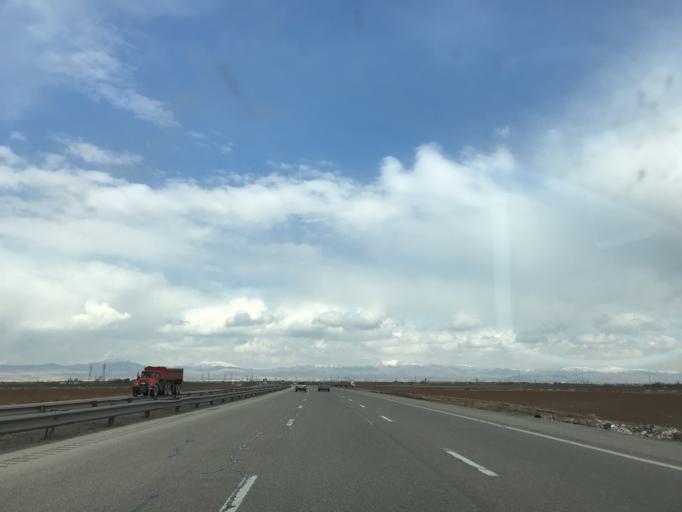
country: IR
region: Qazvin
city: Qazvin
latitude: 36.2376
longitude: 49.9072
